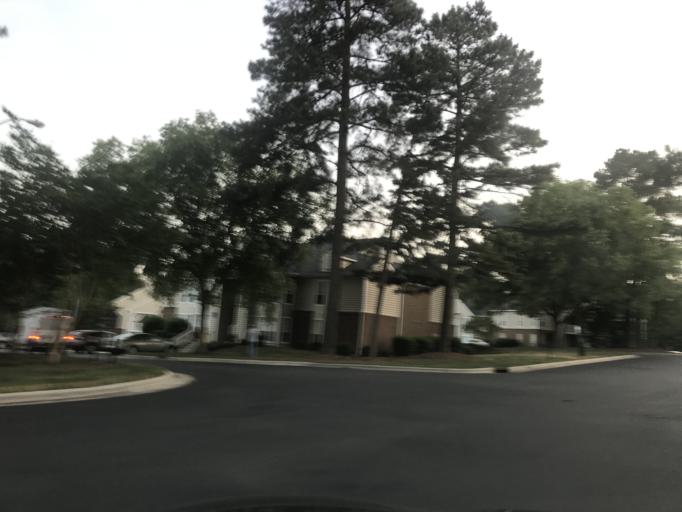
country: US
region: North Carolina
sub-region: Wake County
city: West Raleigh
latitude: 35.8791
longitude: -78.5958
